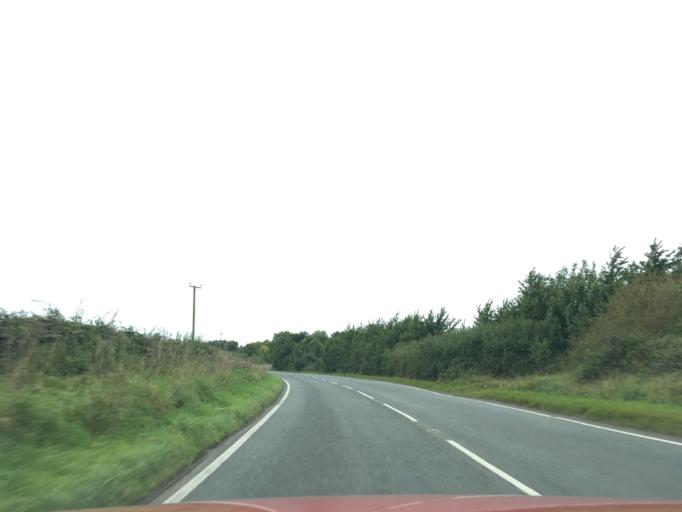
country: GB
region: England
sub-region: South Gloucestershire
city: Almondsbury
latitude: 51.5967
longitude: -2.6038
